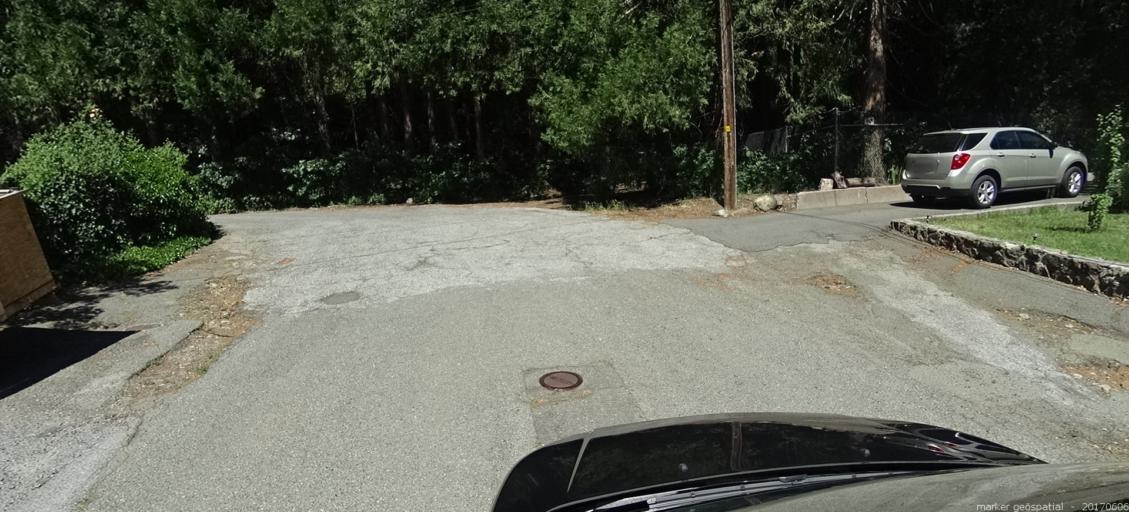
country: US
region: California
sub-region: Siskiyou County
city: Dunsmuir
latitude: 41.2084
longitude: -122.2753
